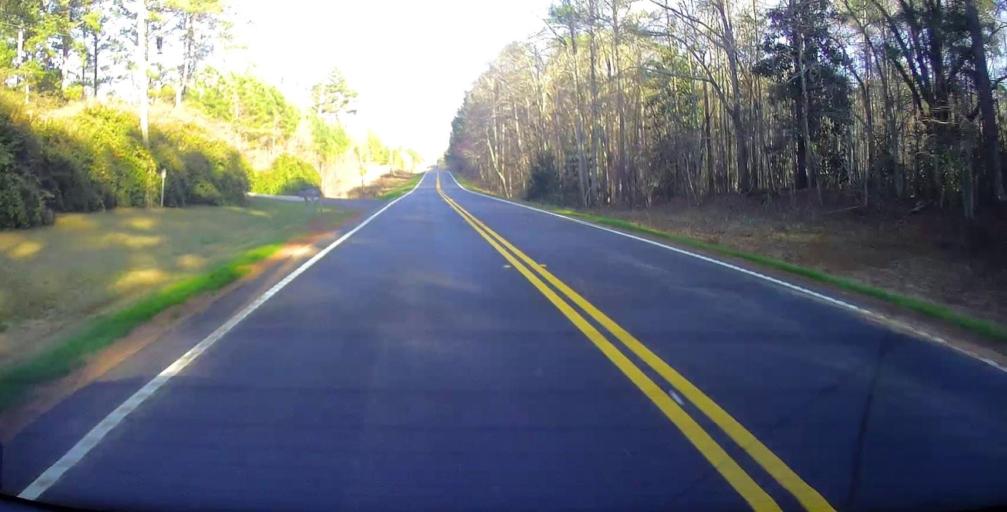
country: US
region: Georgia
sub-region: Harris County
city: Hamilton
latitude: 32.7473
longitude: -85.0023
